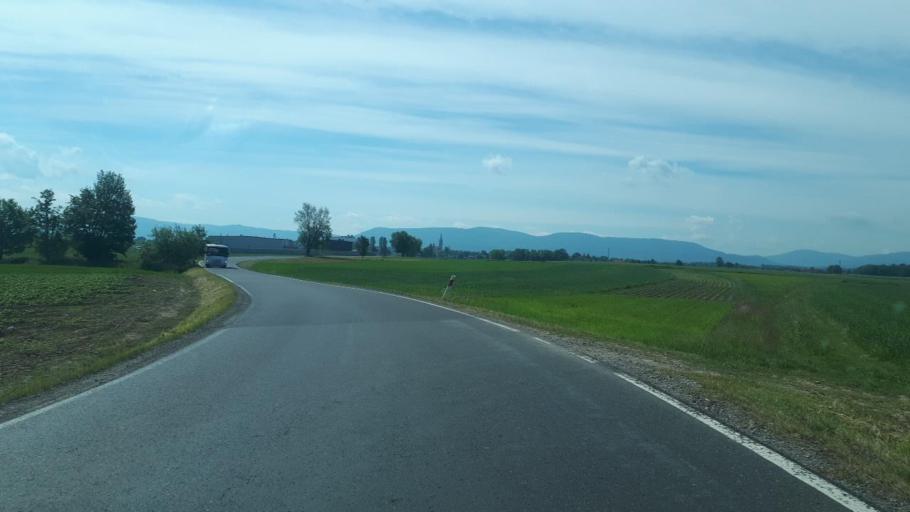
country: PL
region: Silesian Voivodeship
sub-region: Powiat bielski
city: Wilamowice
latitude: 49.9335
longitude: 19.1472
